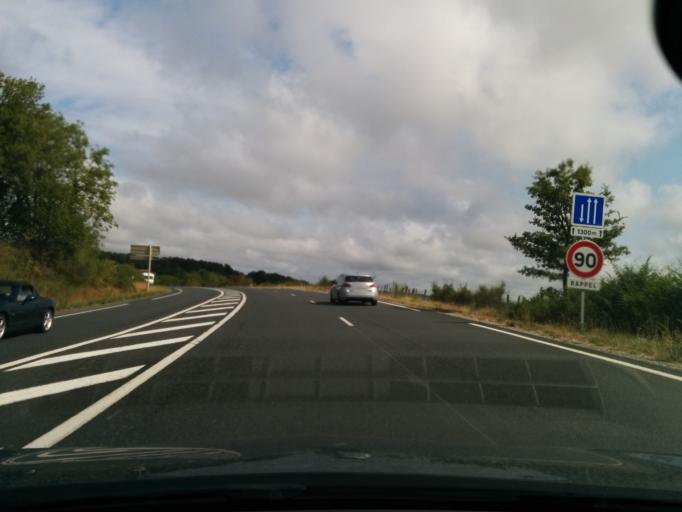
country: FR
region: Midi-Pyrenees
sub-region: Departement du Lot
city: Pradines
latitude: 44.5937
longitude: 1.5157
